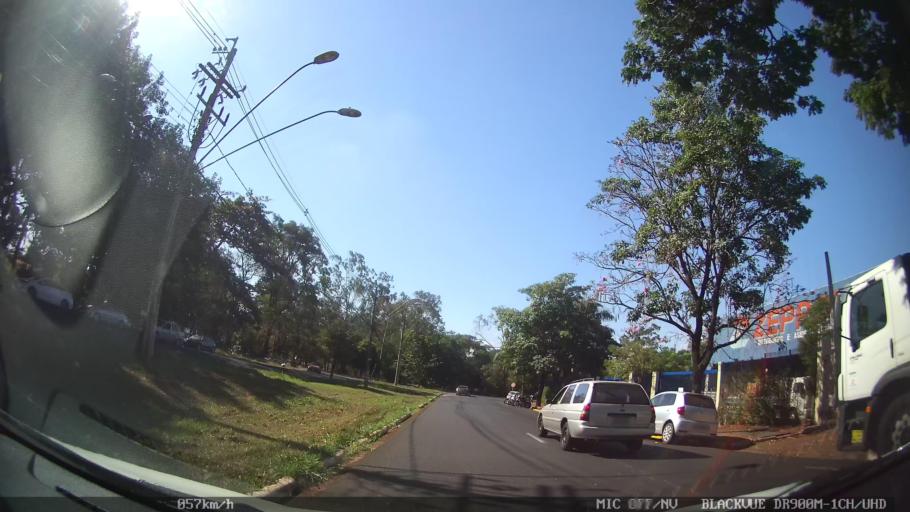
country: BR
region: Sao Paulo
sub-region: Ribeirao Preto
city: Ribeirao Preto
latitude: -21.1945
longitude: -47.7620
